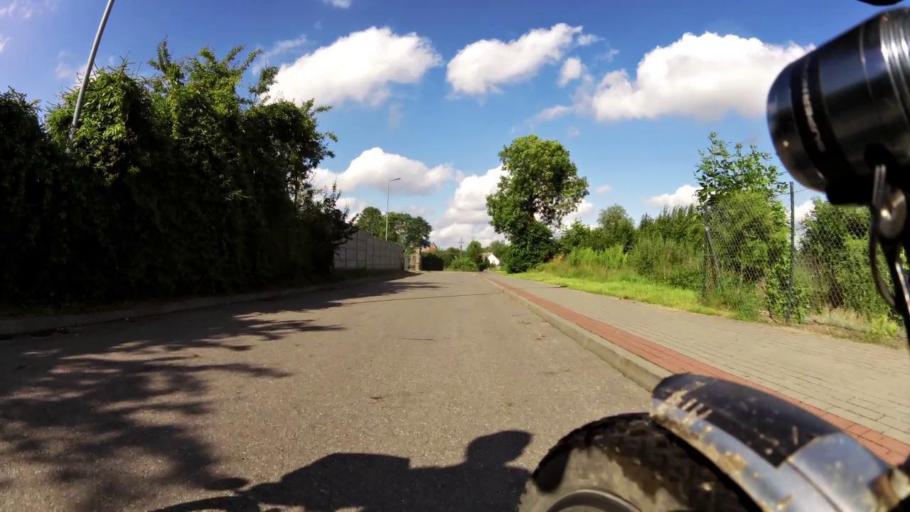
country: PL
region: West Pomeranian Voivodeship
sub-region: Powiat swidwinski
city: Swidwin
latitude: 53.7683
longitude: 15.7629
